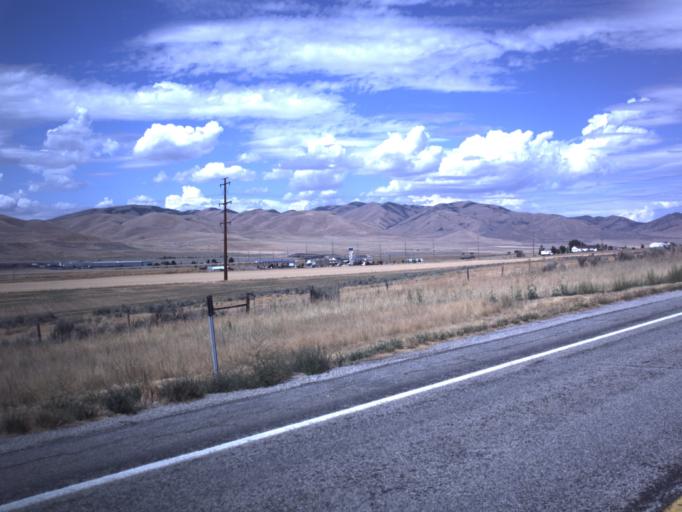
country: US
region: Utah
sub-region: Box Elder County
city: Garland
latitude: 41.8838
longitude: -112.1581
